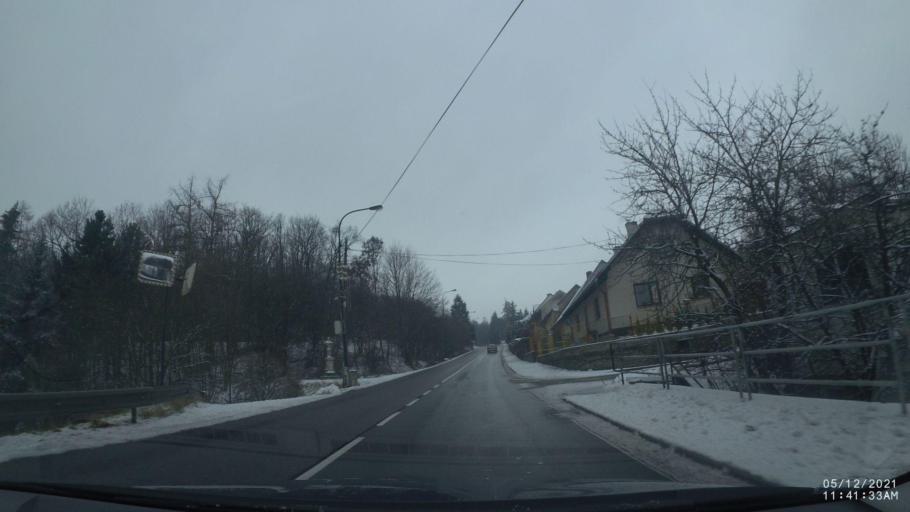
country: CZ
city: Dobruska
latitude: 50.2706
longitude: 16.1946
